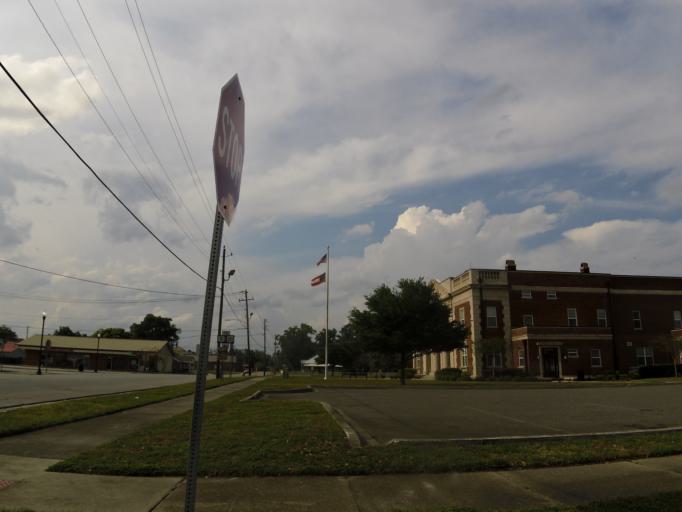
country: US
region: Georgia
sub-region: Charlton County
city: Folkston
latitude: 30.8313
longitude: -82.0051
